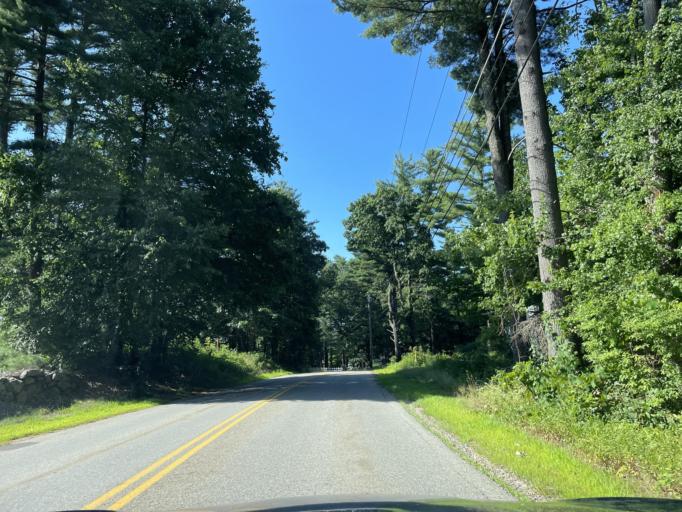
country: US
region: Massachusetts
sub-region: Worcester County
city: Charlton
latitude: 42.1286
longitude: -71.9276
